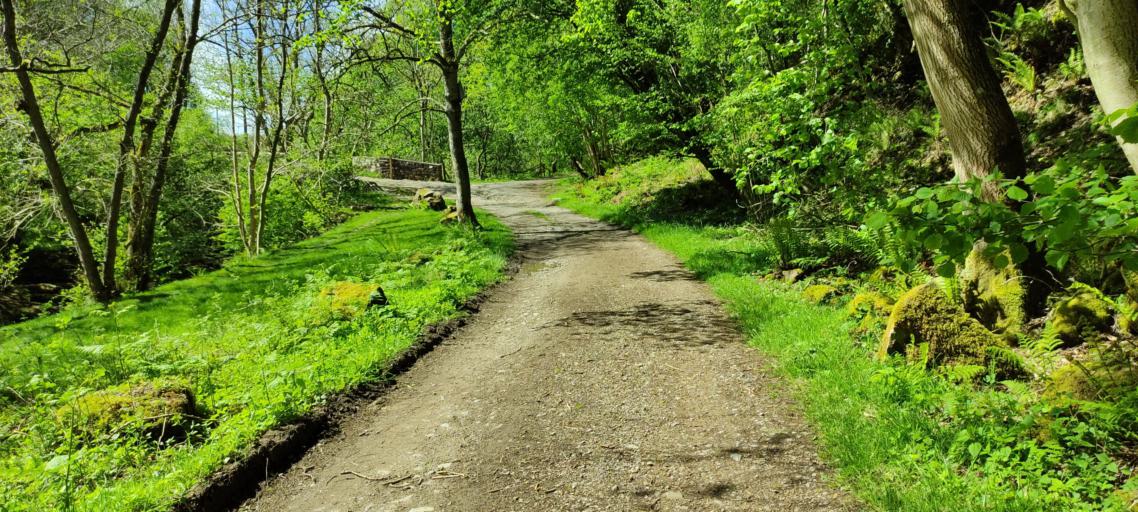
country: GB
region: England
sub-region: Cumbria
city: Brampton
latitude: 54.8945
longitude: -2.6859
